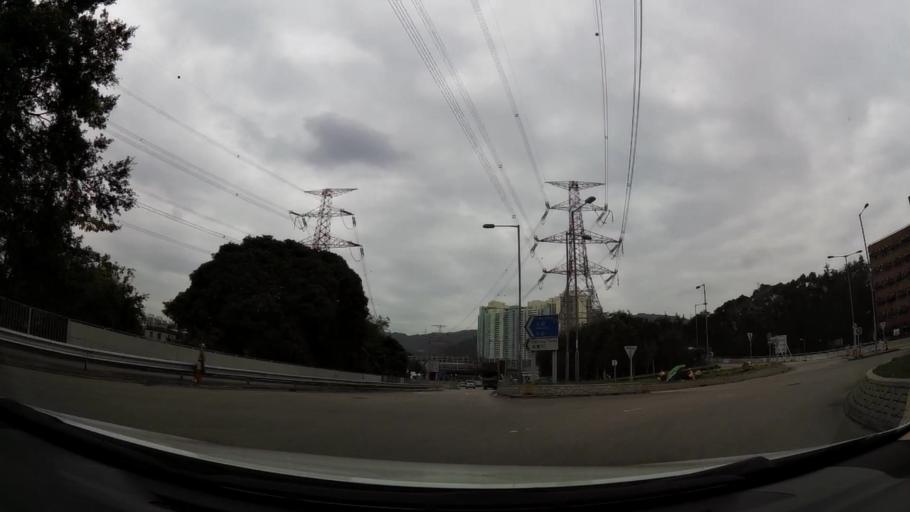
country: HK
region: Tuen Mun
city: Tuen Mun
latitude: 22.4160
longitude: 113.9780
